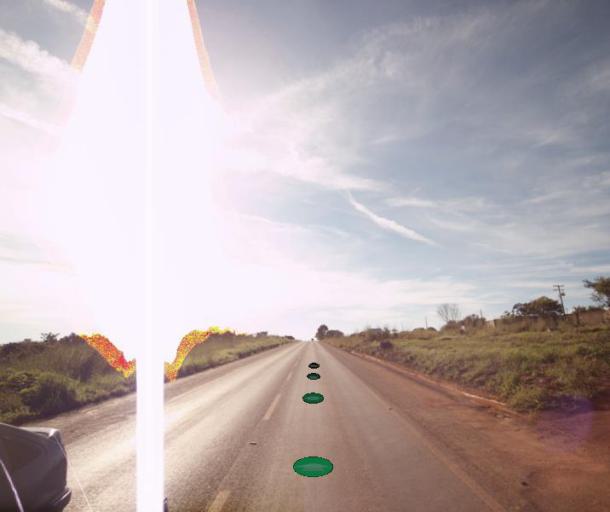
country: BR
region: Federal District
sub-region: Brasilia
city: Brasilia
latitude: -15.7377
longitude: -48.3935
